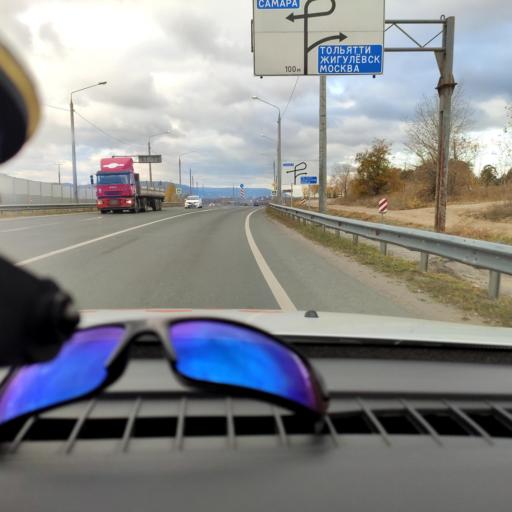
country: RU
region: Samara
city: Volzhskiy
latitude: 53.4340
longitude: 50.1218
